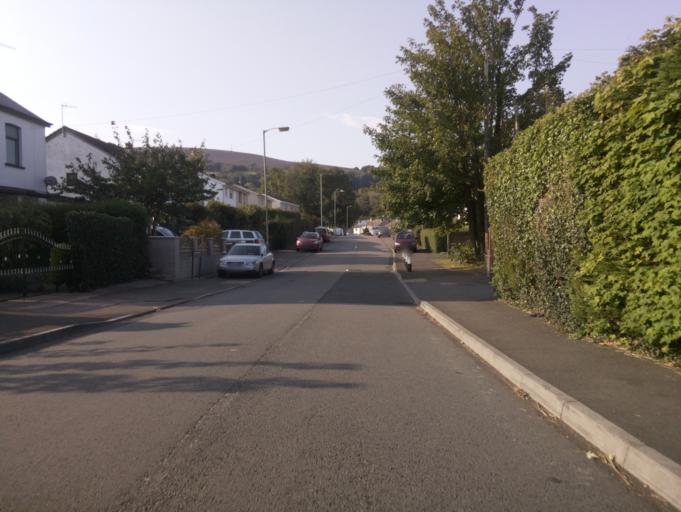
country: GB
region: Wales
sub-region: Torfaen County Borough
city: Cwmbran
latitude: 51.6637
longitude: -3.0349
